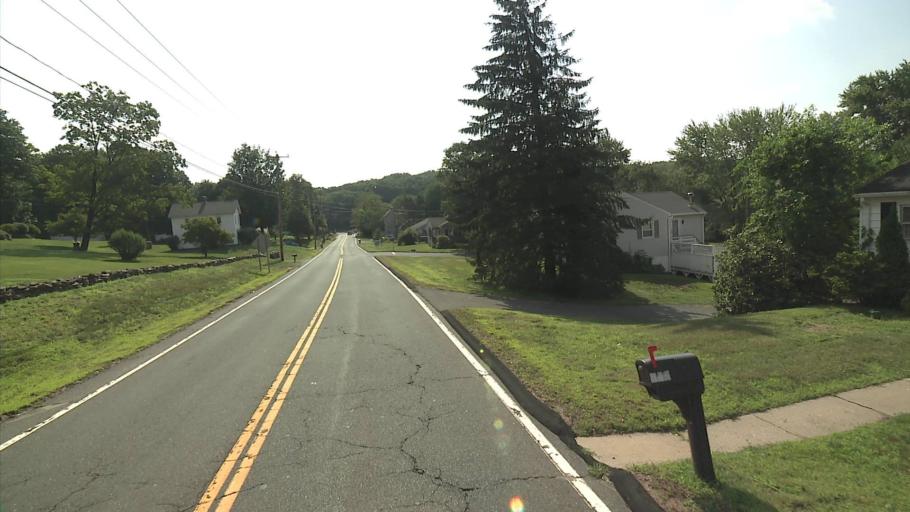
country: US
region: Connecticut
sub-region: New Haven County
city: Wolcott
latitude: 41.5970
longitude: -72.9633
